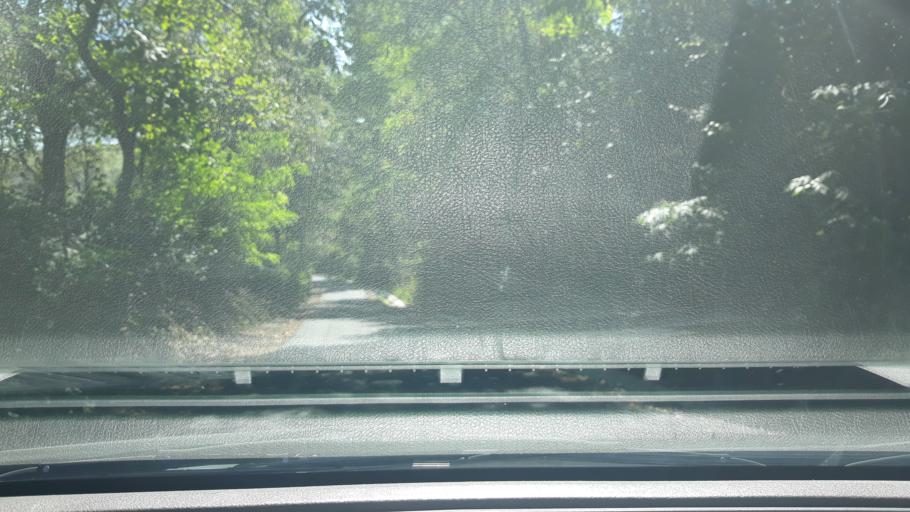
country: RO
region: Salaj
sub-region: Comuna Dobrin
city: Dobrin
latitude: 47.2929
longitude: 23.0837
